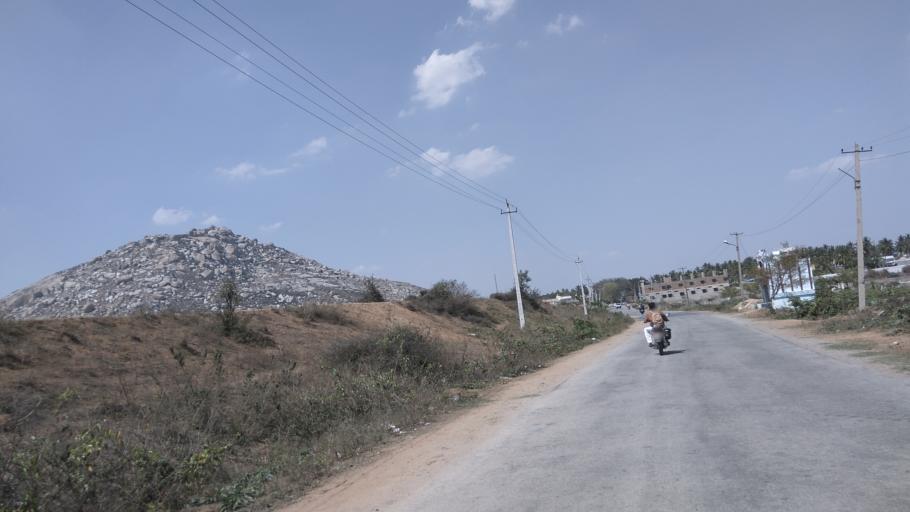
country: IN
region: Karnataka
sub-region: Kolar
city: Mulbagal
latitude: 13.1567
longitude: 78.3832
